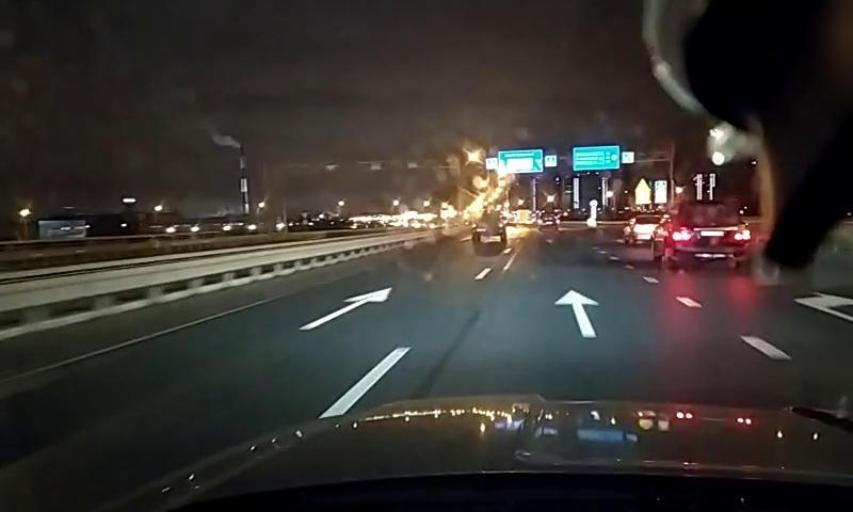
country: RU
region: Leningrad
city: Parnas
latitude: 60.0916
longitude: 30.3680
